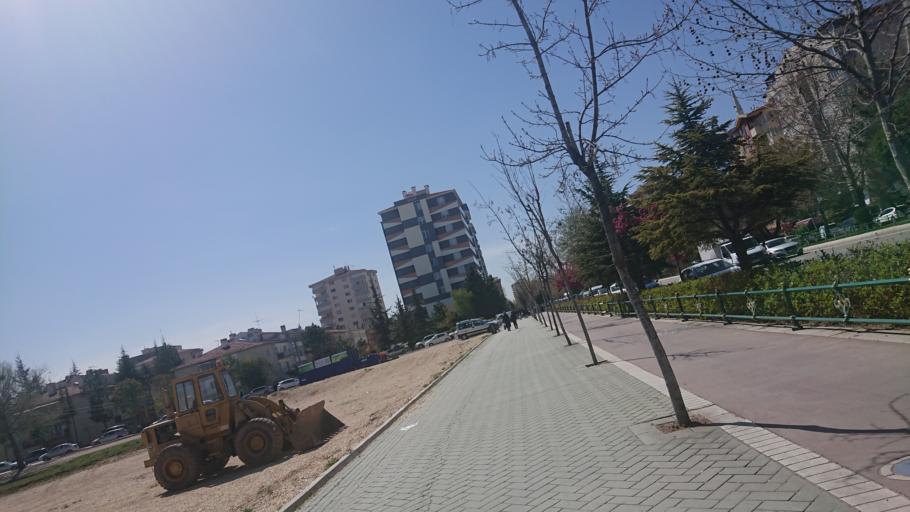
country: TR
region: Eskisehir
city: Eskisehir
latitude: 39.7647
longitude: 30.5073
